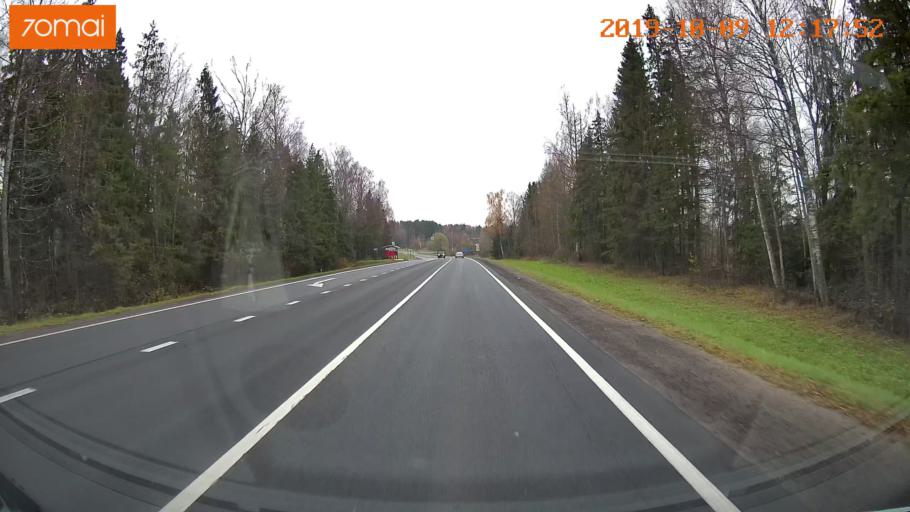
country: RU
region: Jaroslavl
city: Prechistoye
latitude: 58.4505
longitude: 40.3212
